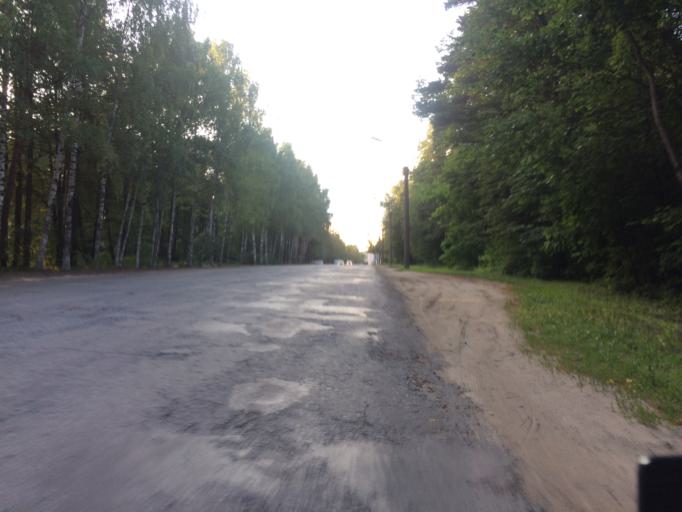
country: RU
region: Mariy-El
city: Yoshkar-Ola
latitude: 56.6241
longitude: 47.9542
